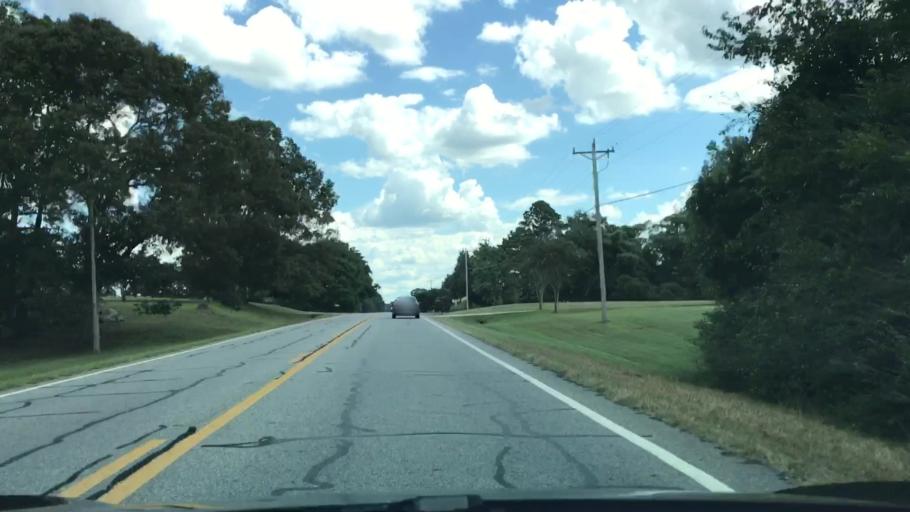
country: US
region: Georgia
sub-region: Oconee County
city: Watkinsville
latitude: 33.8004
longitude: -83.3372
